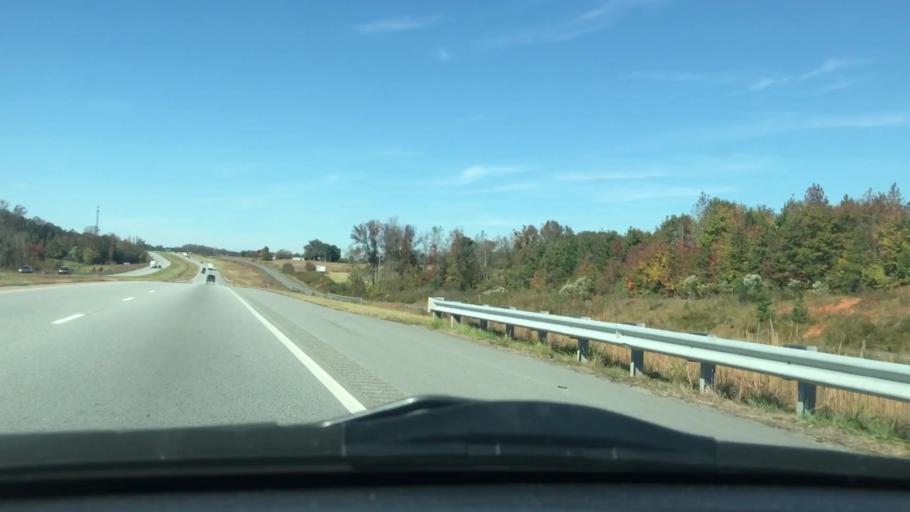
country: US
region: North Carolina
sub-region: Randolph County
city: Randleman
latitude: 35.8618
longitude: -79.8866
